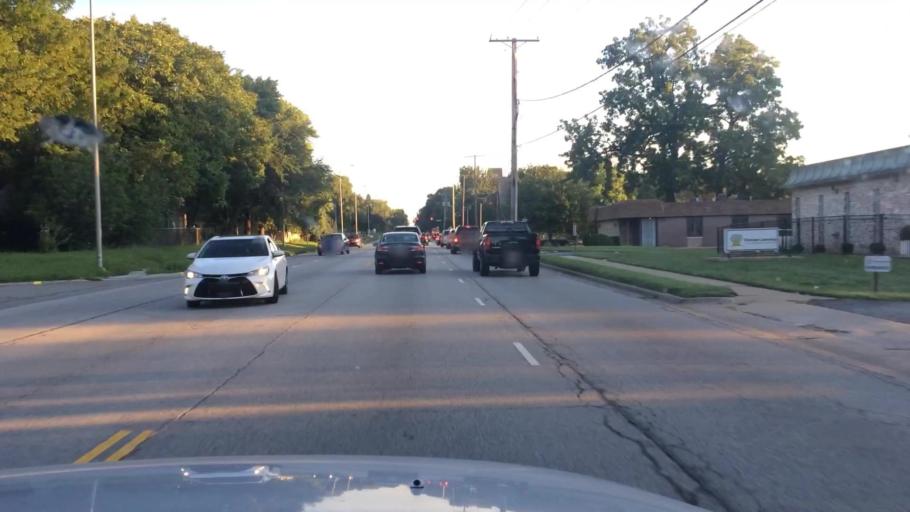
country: US
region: Kansas
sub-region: Johnson County
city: Overland Park
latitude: 38.9977
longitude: -94.6677
